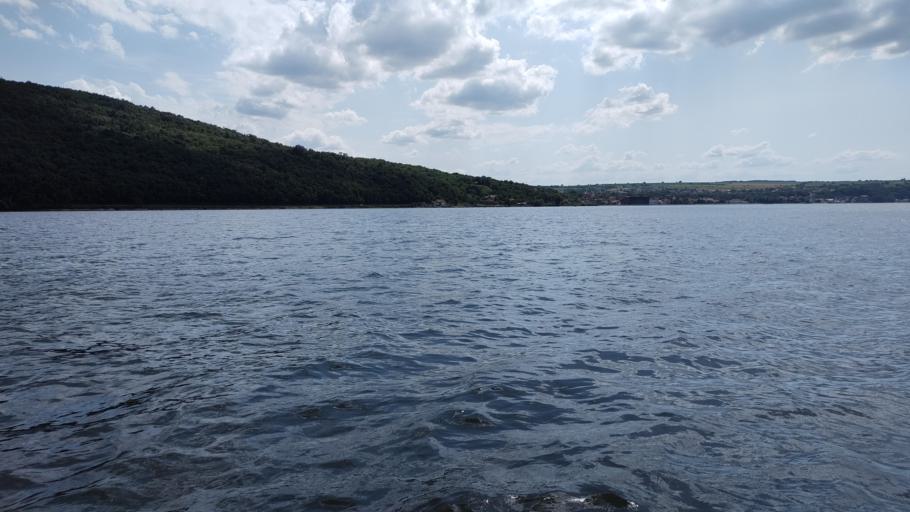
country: RS
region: Central Serbia
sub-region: Branicevski Okrug
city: Golubac
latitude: 44.6593
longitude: 21.6525
